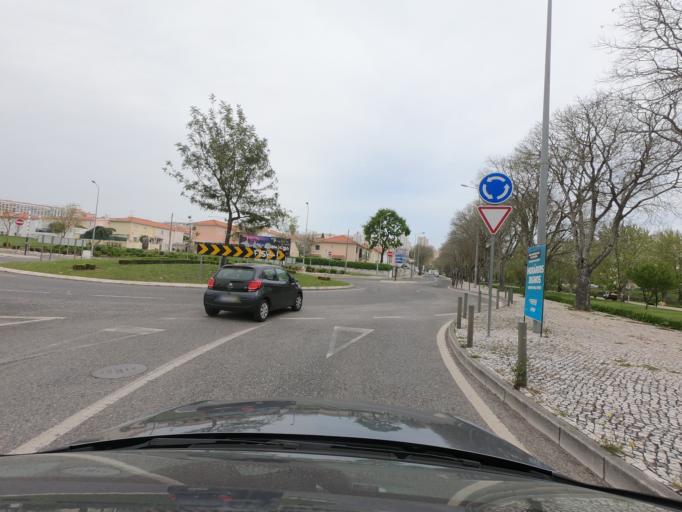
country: PT
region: Lisbon
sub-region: Sintra
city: Queluz
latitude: 38.7541
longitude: -9.2597
